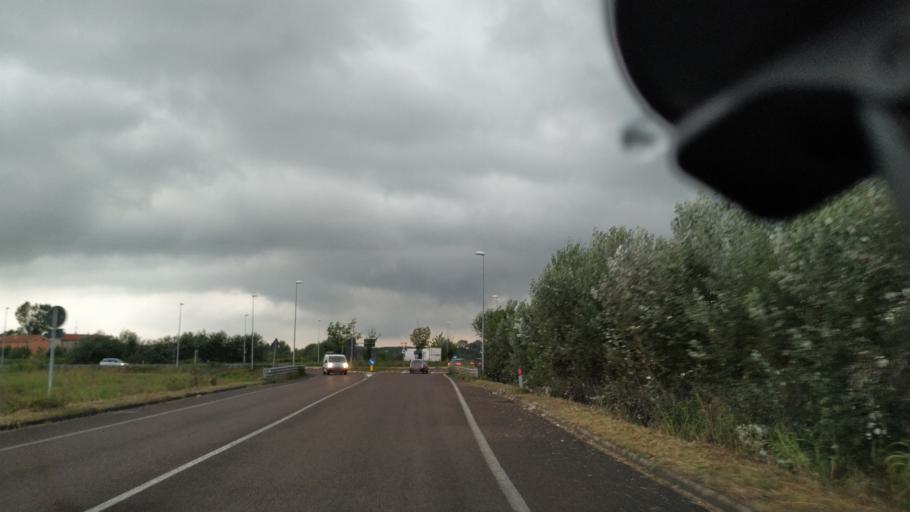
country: IT
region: Emilia-Romagna
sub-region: Provincia di Modena
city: Nonantola
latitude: 44.6856
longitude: 11.0235
